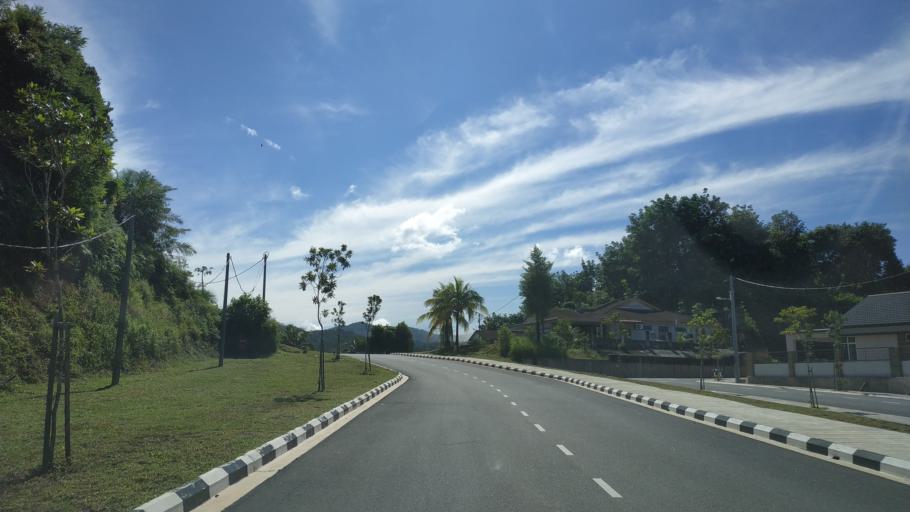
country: MY
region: Kedah
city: Kulim
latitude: 5.3391
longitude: 100.5344
